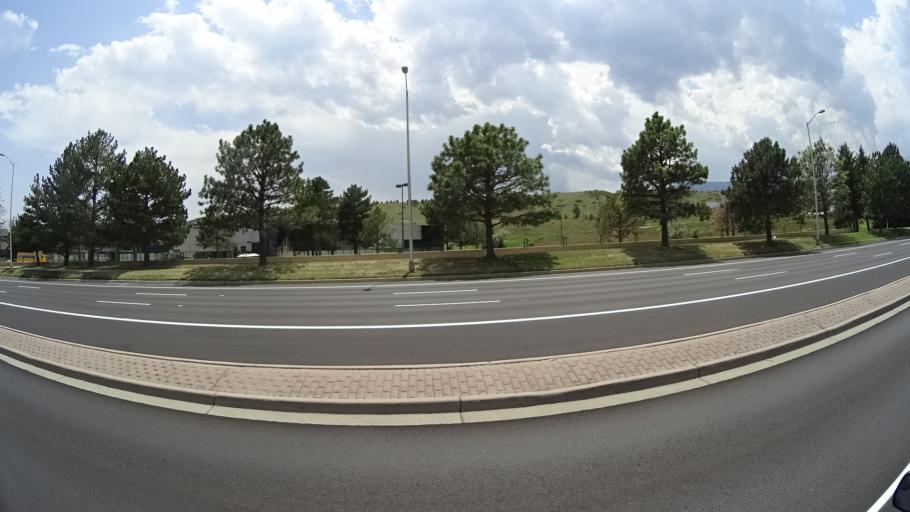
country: US
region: Colorado
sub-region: El Paso County
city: Manitou Springs
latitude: 38.8967
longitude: -104.8674
